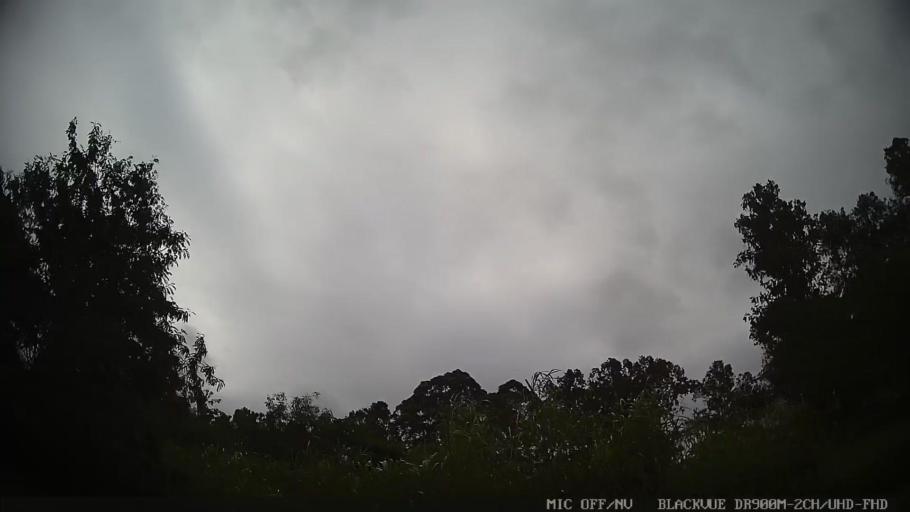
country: BR
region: Sao Paulo
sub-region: Osasco
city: Osasco
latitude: -23.4771
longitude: -46.7328
